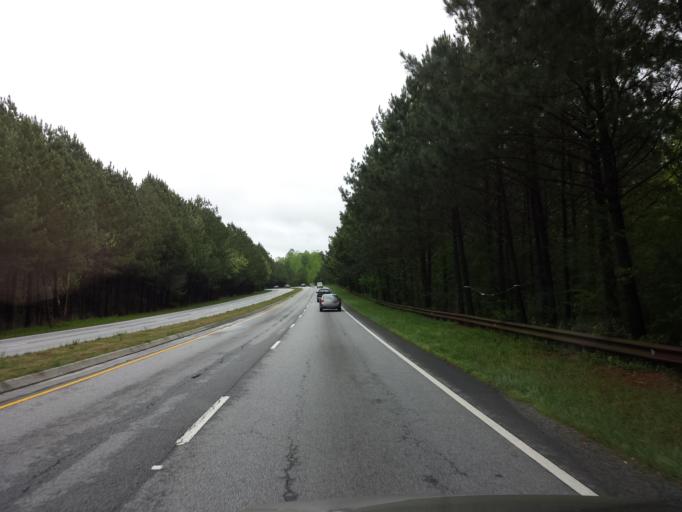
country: US
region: Georgia
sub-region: Cobb County
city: Mableton
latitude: 33.8470
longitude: -84.5498
